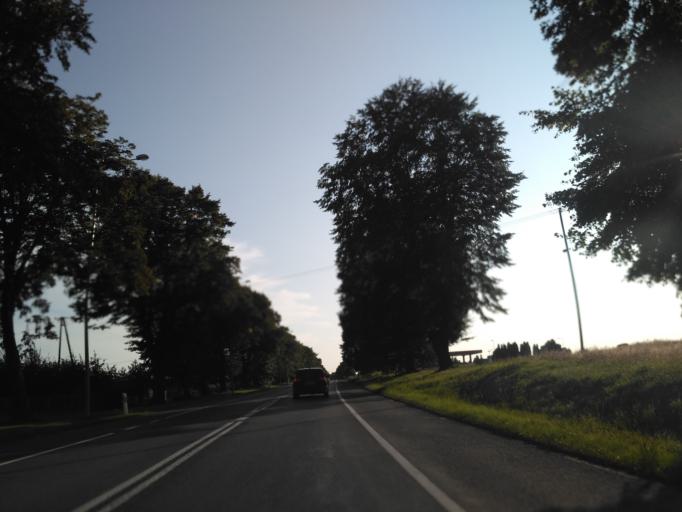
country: PL
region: Lublin Voivodeship
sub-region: Powiat lubelski
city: Jablonna
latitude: 51.1085
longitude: 22.5892
